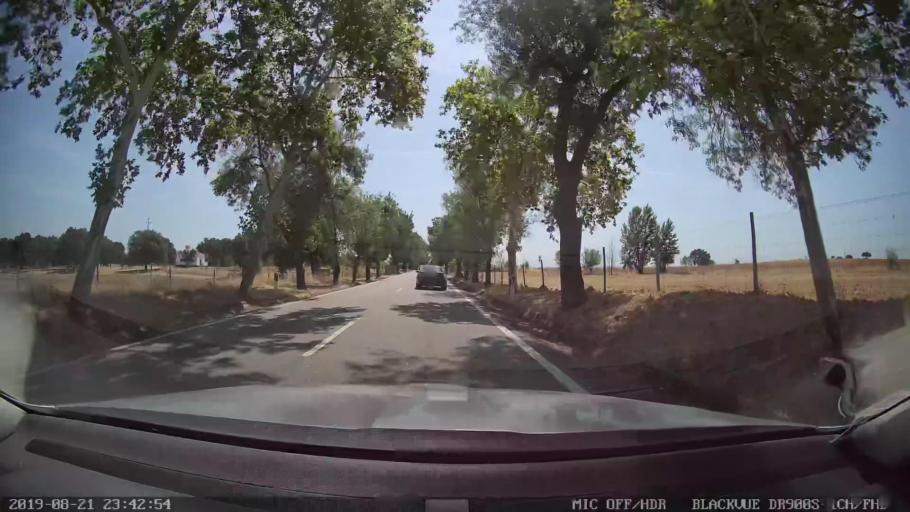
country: PT
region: Castelo Branco
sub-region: Idanha-A-Nova
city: Idanha-a-Nova
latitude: 39.8528
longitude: -7.3044
